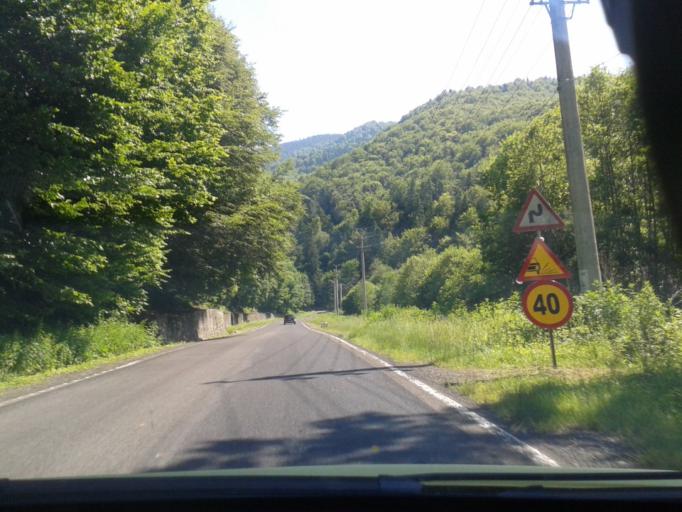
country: RO
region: Sibiu
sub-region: Comuna Cartisoara
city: Cartisoara
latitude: 45.6700
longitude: 24.5776
